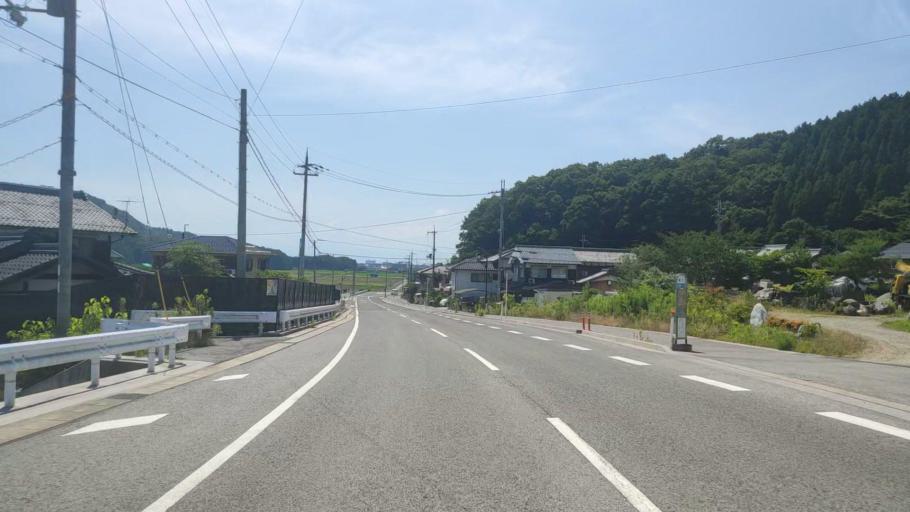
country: JP
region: Shiga Prefecture
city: Nagahama
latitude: 35.3872
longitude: 136.3303
